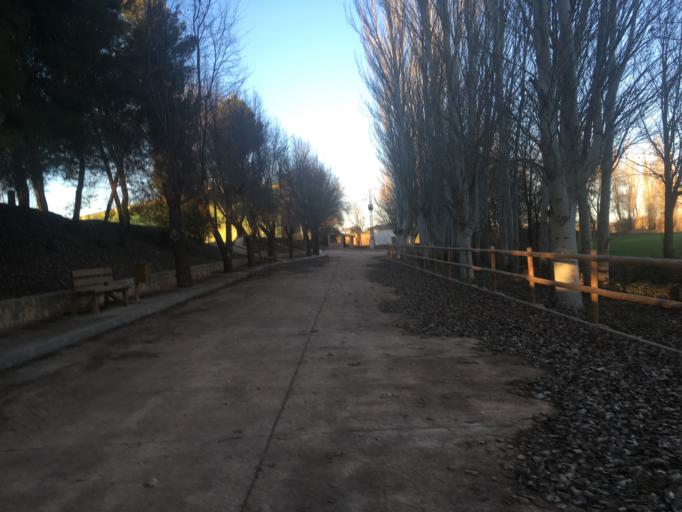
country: ES
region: Castille-La Mancha
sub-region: Provincia de Cuenca
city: Atalaya del Canavate
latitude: 39.5532
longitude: -2.2522
